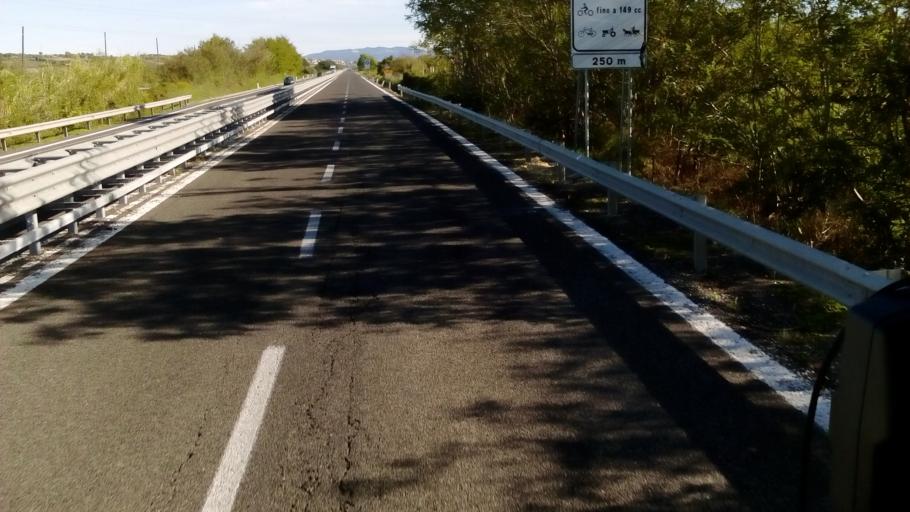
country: IT
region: Latium
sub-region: Provincia di Viterbo
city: Tarquinia
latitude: 42.2815
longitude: 11.6943
